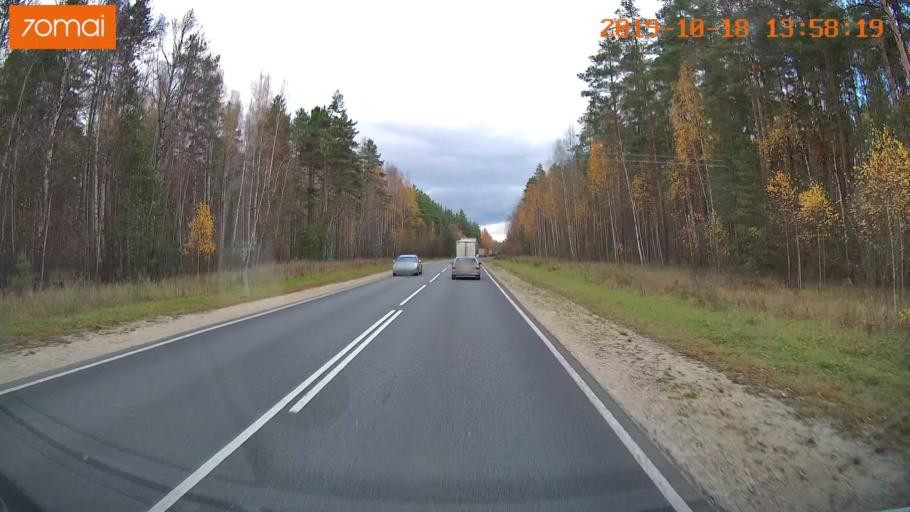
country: RU
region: Rjazan
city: Spas-Klepiki
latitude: 55.0835
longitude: 40.0533
